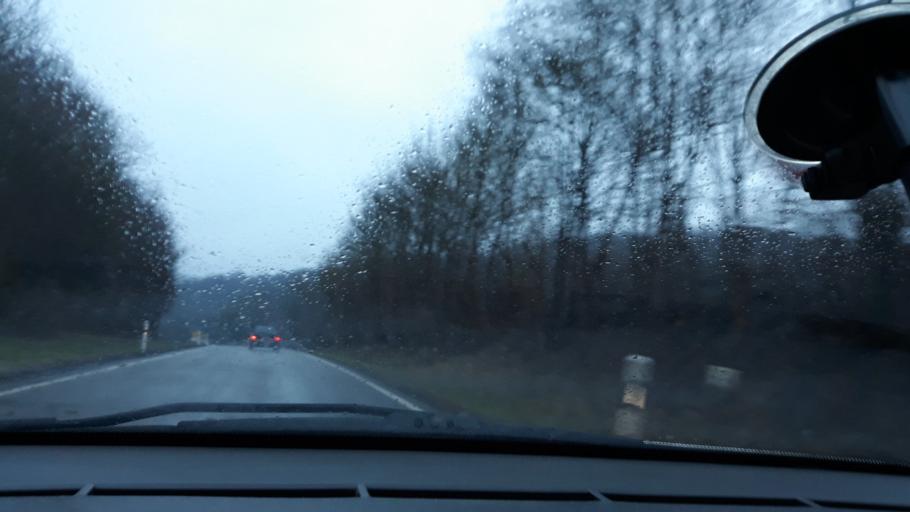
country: DE
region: Saarland
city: Kleinblittersdorf
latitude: 49.2039
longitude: 7.0484
